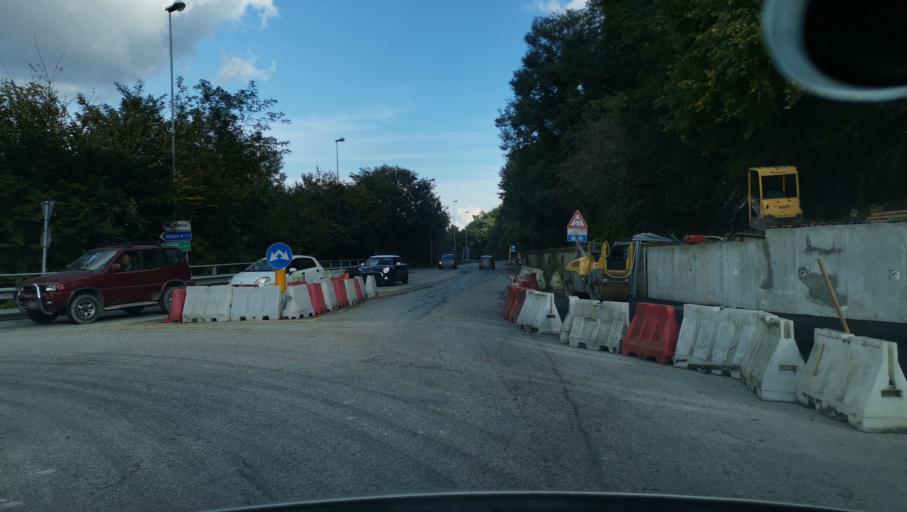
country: IT
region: Piedmont
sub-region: Provincia di Torino
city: Castagneto Po
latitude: 45.1774
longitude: 7.8907
